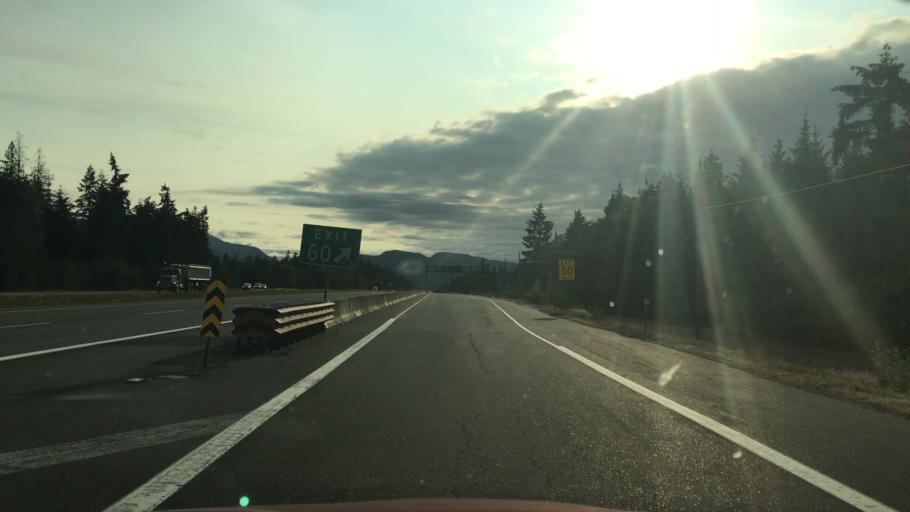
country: CA
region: British Columbia
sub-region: Regional District of Nanaimo
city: Parksville
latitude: 49.3256
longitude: -124.4323
